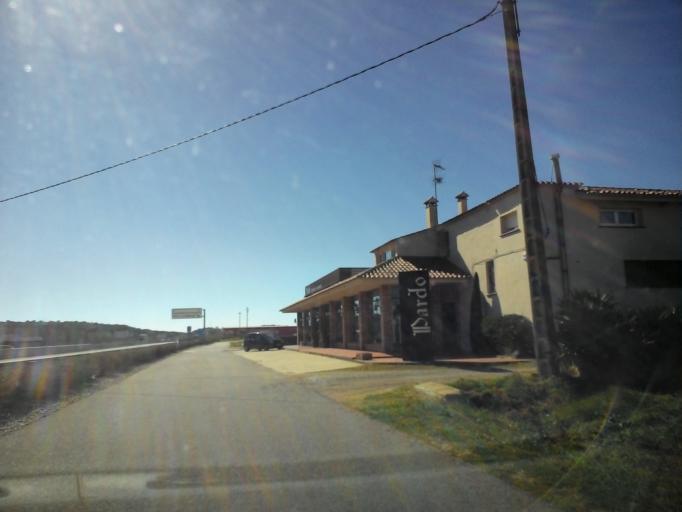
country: ES
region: Catalonia
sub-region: Provincia de Girona
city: Palamos
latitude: 41.8744
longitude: 3.1389
